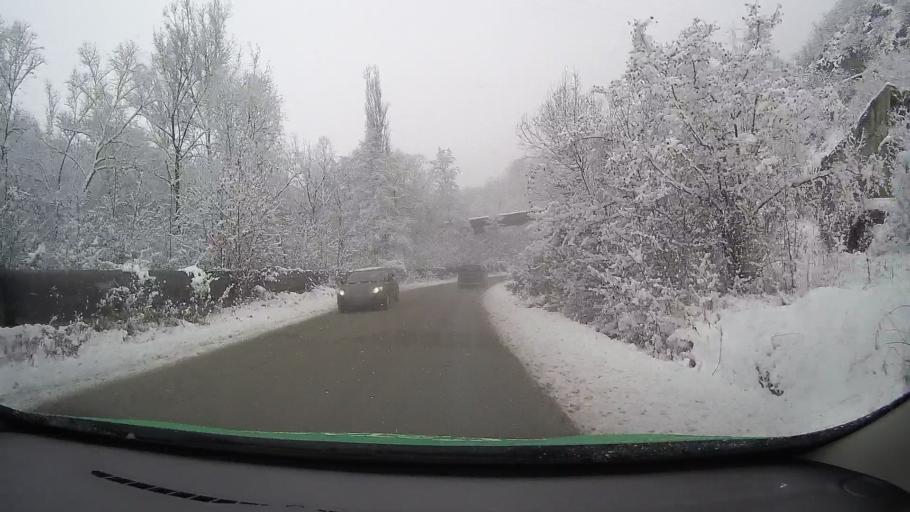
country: RO
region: Hunedoara
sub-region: Comuna Teliucu Inferior
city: Teliucu Inferior
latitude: 45.7278
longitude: 22.8804
